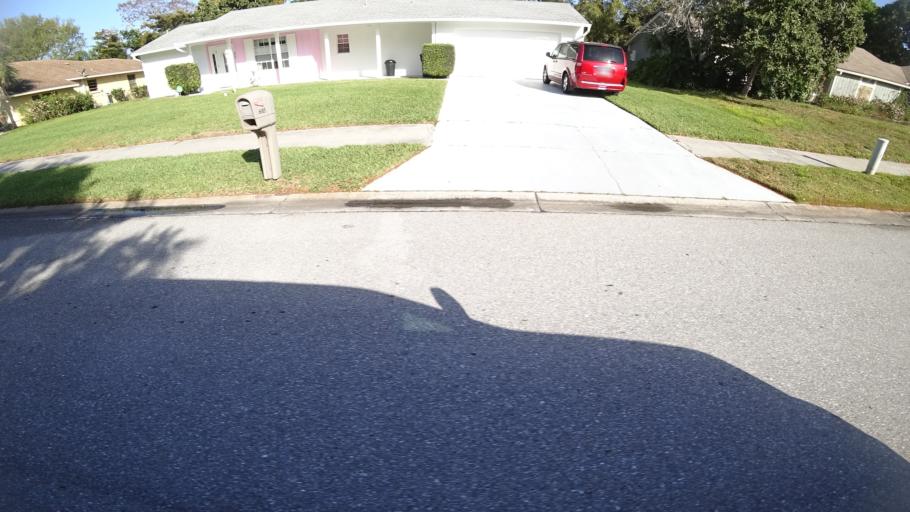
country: US
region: Florida
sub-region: Manatee County
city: Whitfield
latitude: 27.4125
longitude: -82.5608
